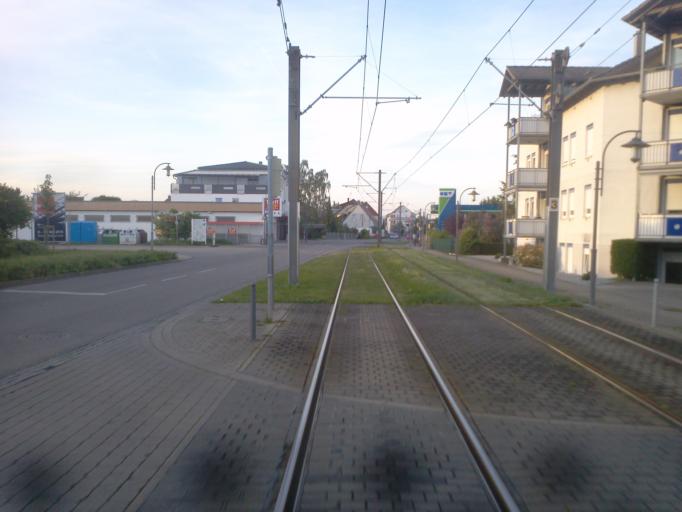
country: DE
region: Baden-Wuerttemberg
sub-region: Karlsruhe Region
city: Weingarten
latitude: 49.0583
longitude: 8.4678
